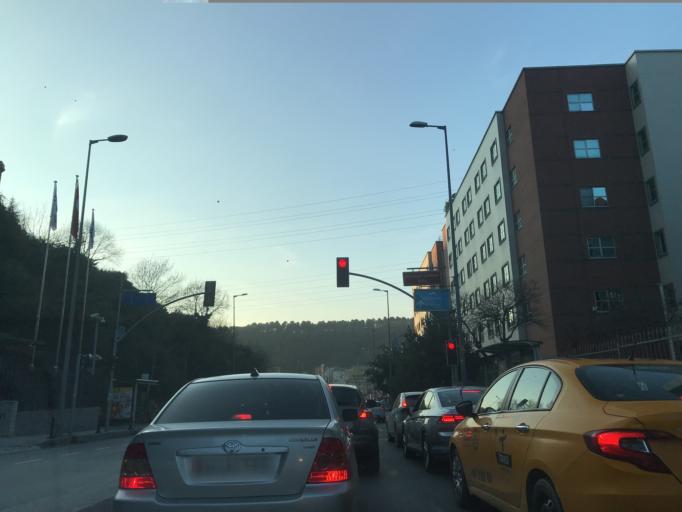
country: TR
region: Istanbul
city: Sisli
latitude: 41.1110
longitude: 29.0005
